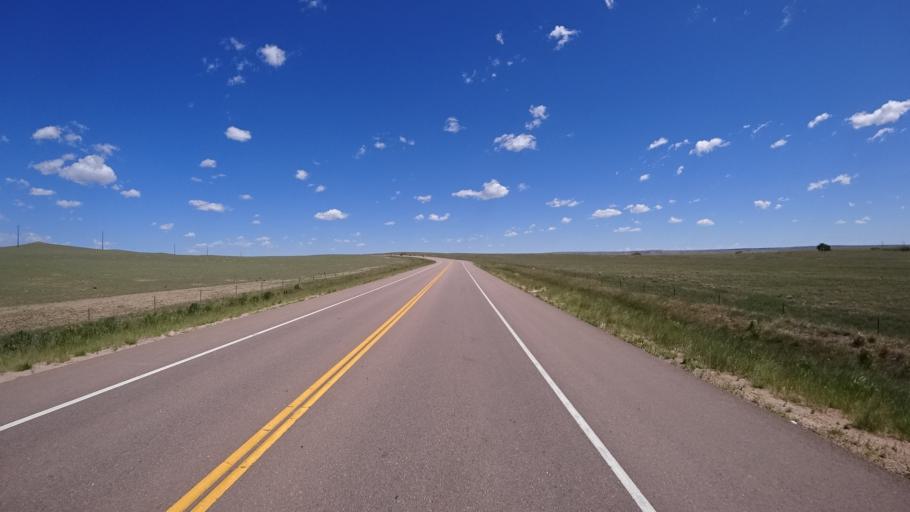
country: US
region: Colorado
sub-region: El Paso County
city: Security-Widefield
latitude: 38.7891
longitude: -104.6579
